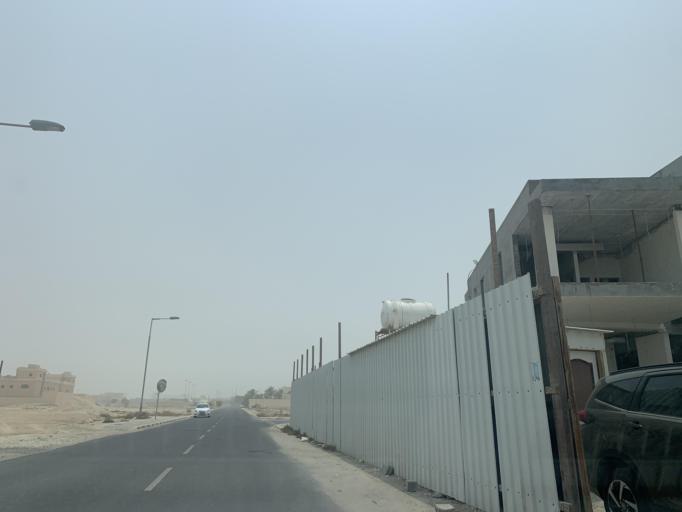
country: BH
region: Central Governorate
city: Madinat Hamad
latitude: 26.1697
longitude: 50.4816
